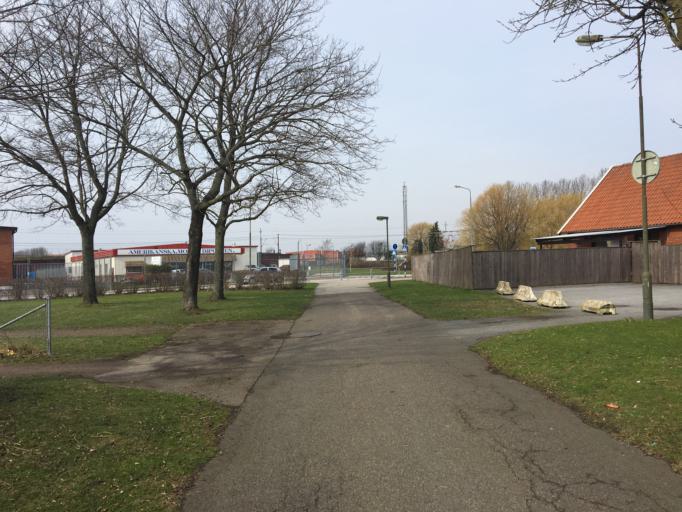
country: SE
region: Skane
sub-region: Burlovs Kommun
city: Arloev
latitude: 55.6391
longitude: 13.0802
